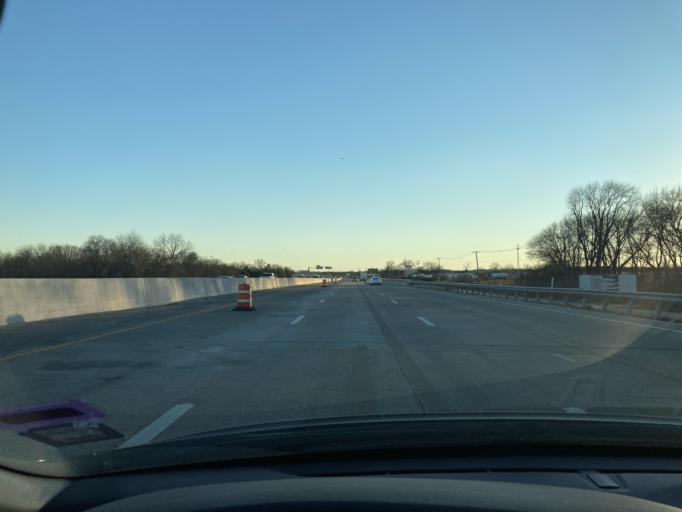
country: US
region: Texas
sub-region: Ellis County
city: Oak Leaf
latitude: 32.4696
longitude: -96.8391
